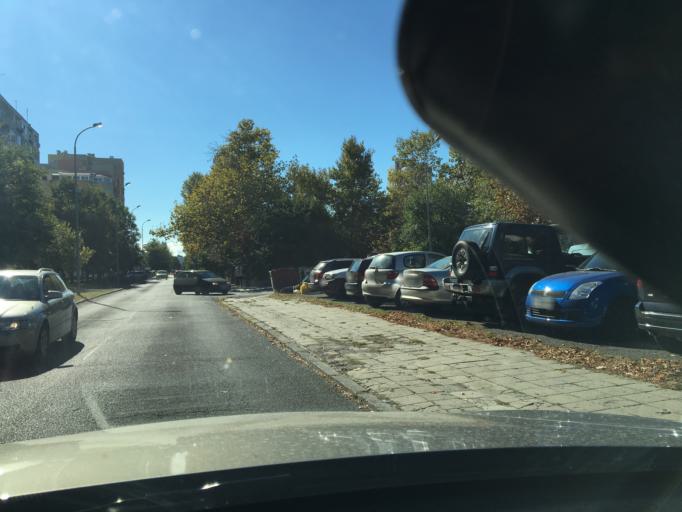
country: BG
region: Burgas
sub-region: Obshtina Burgas
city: Burgas
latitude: 42.5234
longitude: 27.4486
